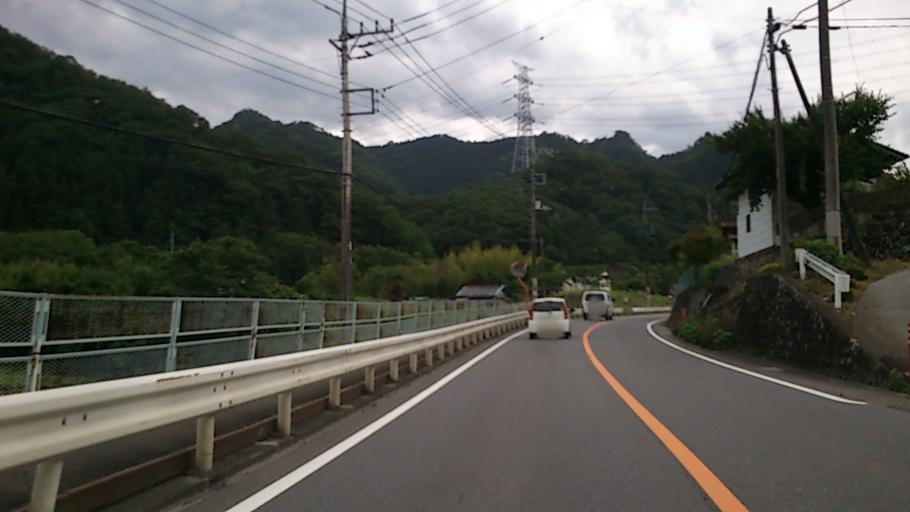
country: JP
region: Gunma
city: Tomioka
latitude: 36.2156
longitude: 138.8034
